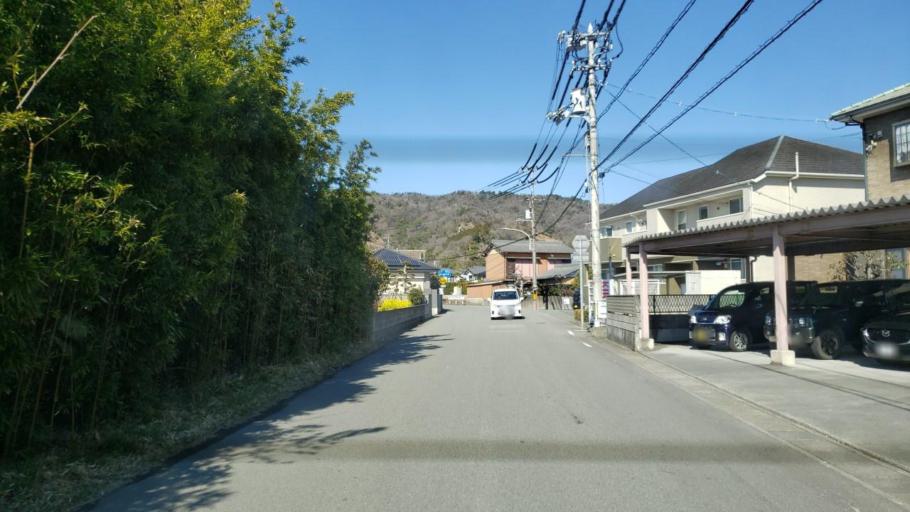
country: JP
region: Tokushima
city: Narutocho-mitsuishi
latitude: 34.1546
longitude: 134.5316
